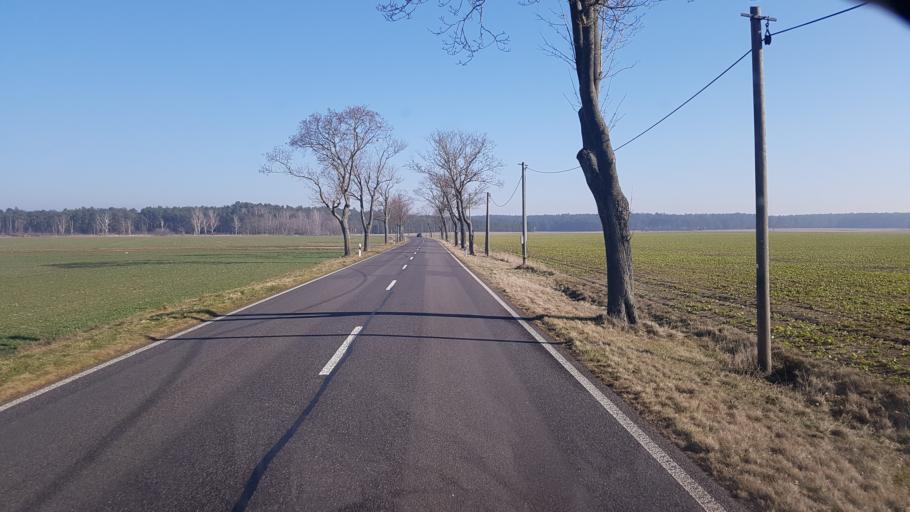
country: DE
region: Brandenburg
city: Ihlow
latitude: 51.8073
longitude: 13.3132
